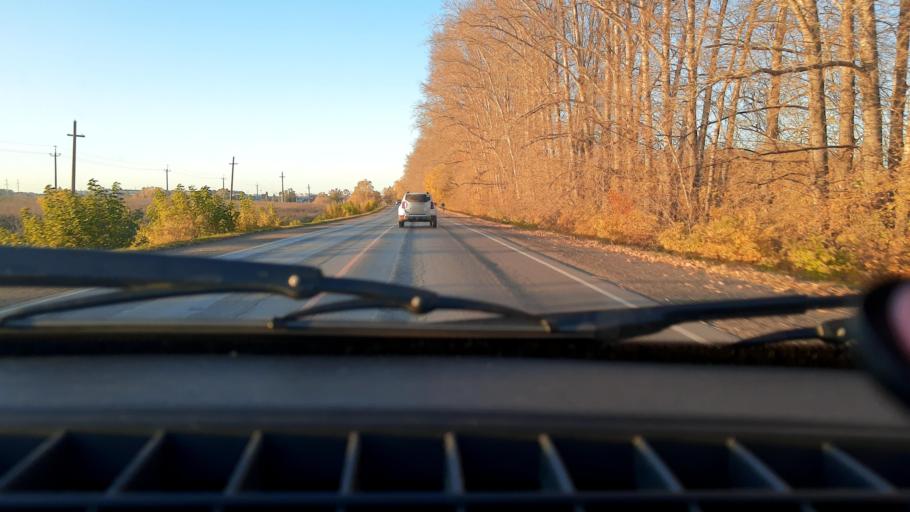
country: RU
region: Bashkortostan
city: Avdon
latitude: 54.7287
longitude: 55.8055
